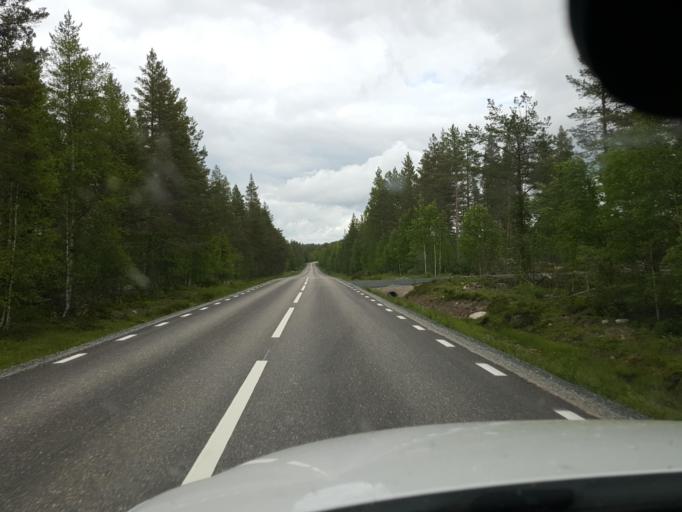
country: SE
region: Gaevleborg
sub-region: Ljusdals Kommun
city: Farila
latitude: 61.7435
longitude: 15.3554
